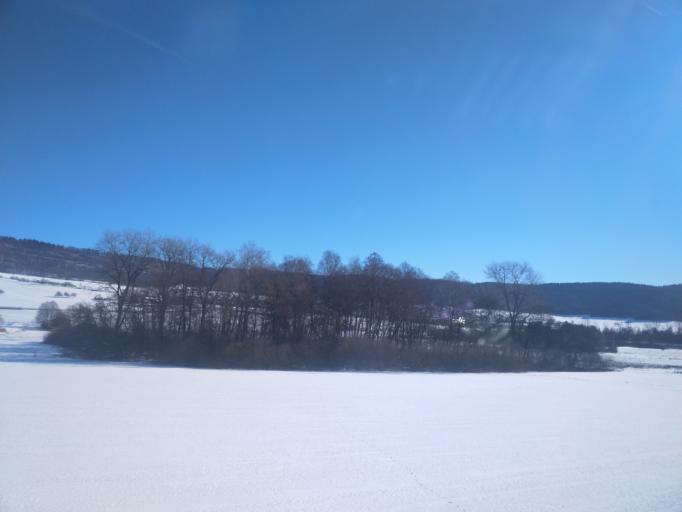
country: DE
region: Baden-Wuerttemberg
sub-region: Freiburg Region
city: Balgheim
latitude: 48.0584
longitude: 8.7711
